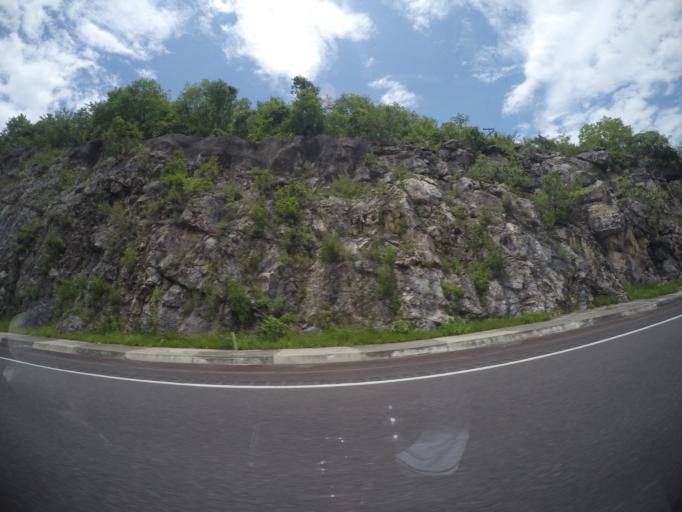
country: MX
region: Guerrero
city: Huitziltepec
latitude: 17.7681
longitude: -99.4801
